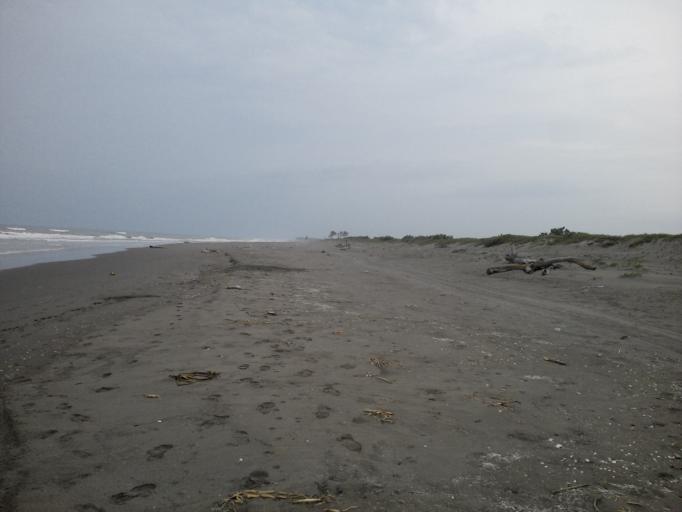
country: MX
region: Veracruz
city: Nautla
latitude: 20.2129
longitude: -96.7590
